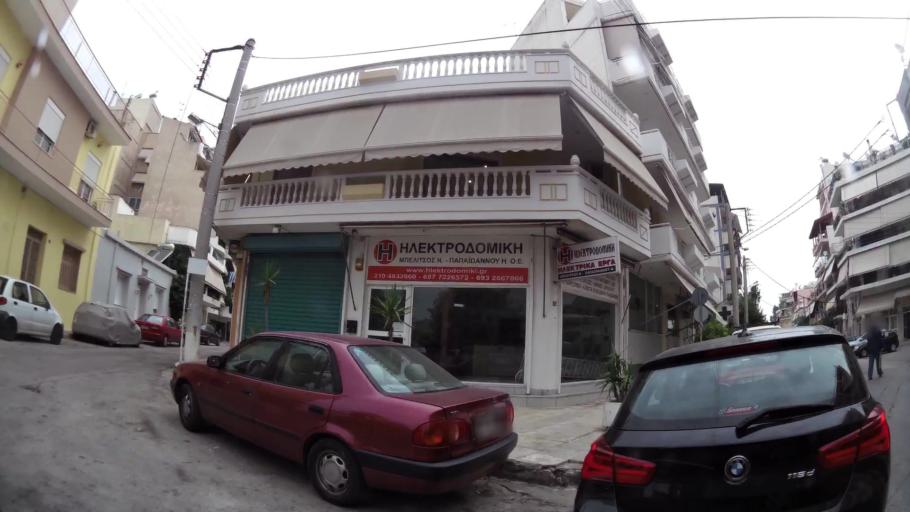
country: GR
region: Attica
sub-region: Nomos Piraios
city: Agios Ioannis Rentis
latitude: 37.9527
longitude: 23.6593
